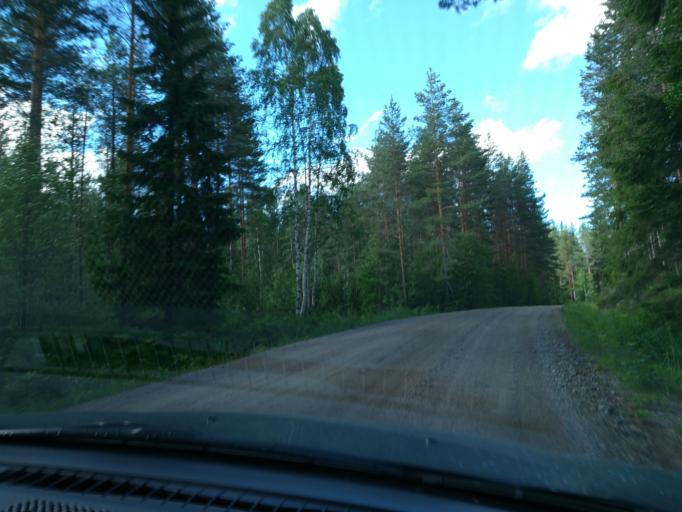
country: FI
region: South Karelia
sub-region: Lappeenranta
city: Savitaipale
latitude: 61.3093
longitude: 27.6300
